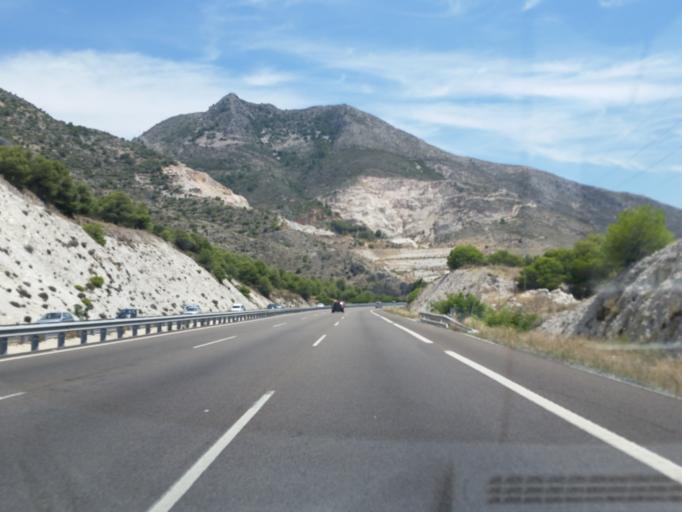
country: ES
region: Andalusia
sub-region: Provincia de Malaga
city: Benalmadena
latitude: 36.6013
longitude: -4.5714
